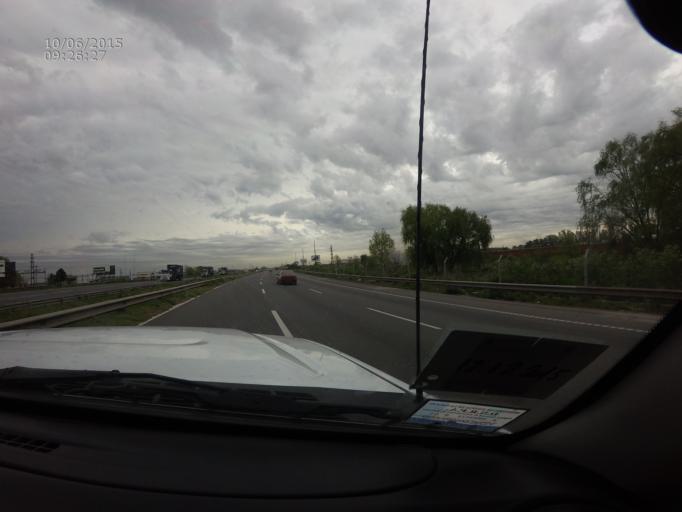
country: AR
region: Buenos Aires
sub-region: Partido de Campana
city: Campana
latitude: -34.1763
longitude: -58.9770
